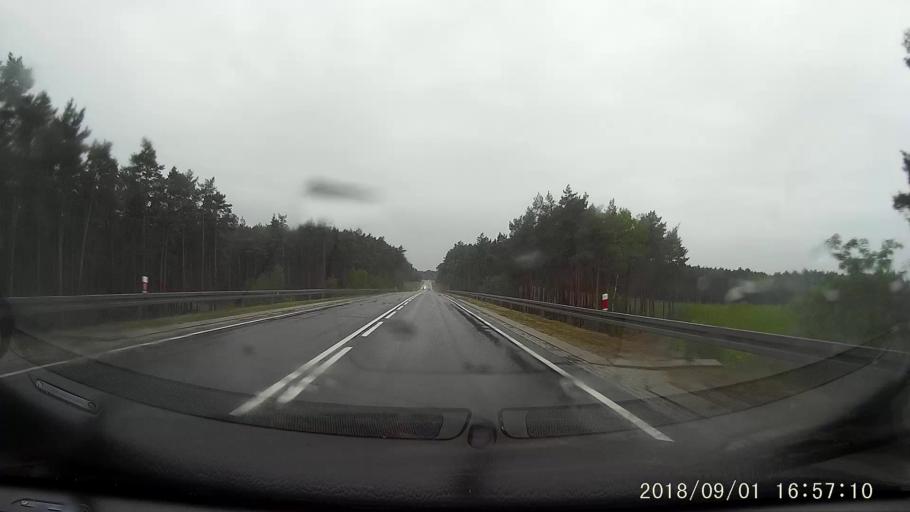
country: PL
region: Lubusz
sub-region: Powiat zielonogorski
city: Swidnica
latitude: 51.9339
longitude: 15.4263
